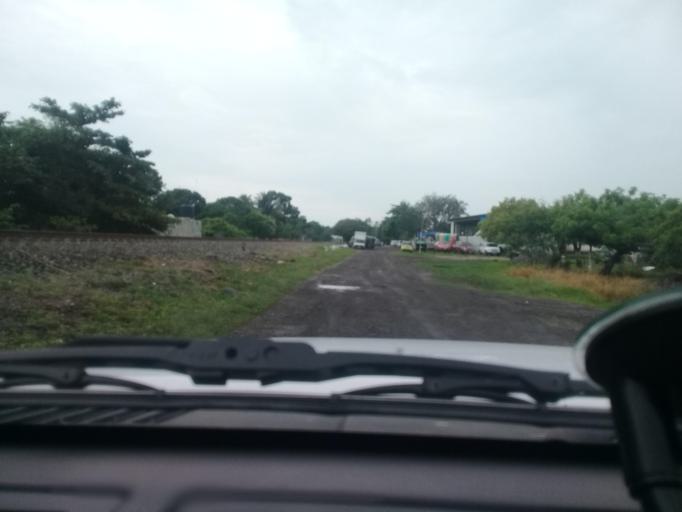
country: MX
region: Veracruz
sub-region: Puente Nacional
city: Cabezas
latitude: 19.3587
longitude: -96.4164
